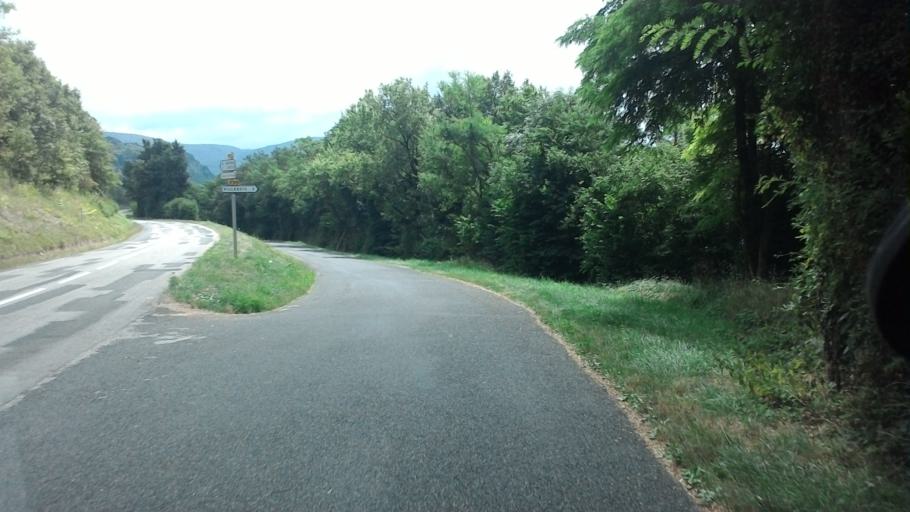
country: FR
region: Rhone-Alpes
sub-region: Departement de l'Ain
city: Sault-Brenaz
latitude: 45.8755
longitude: 5.4009
